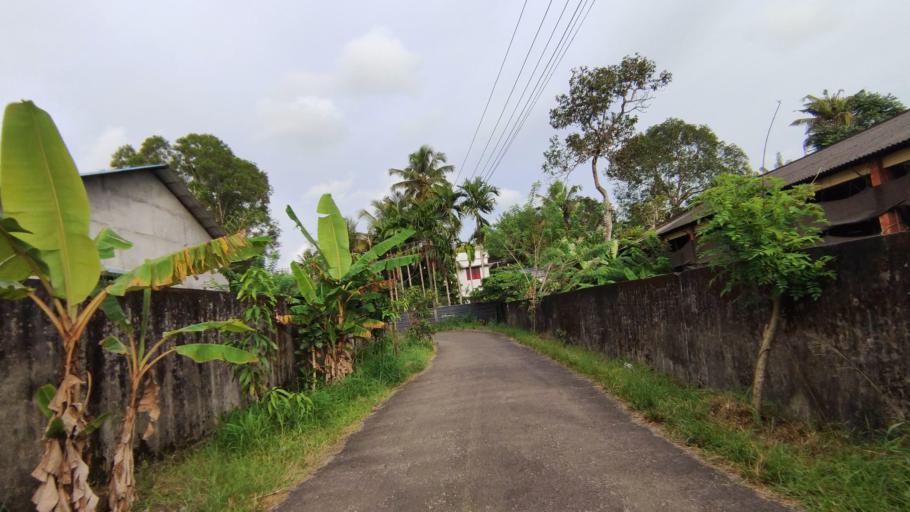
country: IN
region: Kerala
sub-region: Alappuzha
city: Shertallai
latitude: 9.6180
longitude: 76.3471
